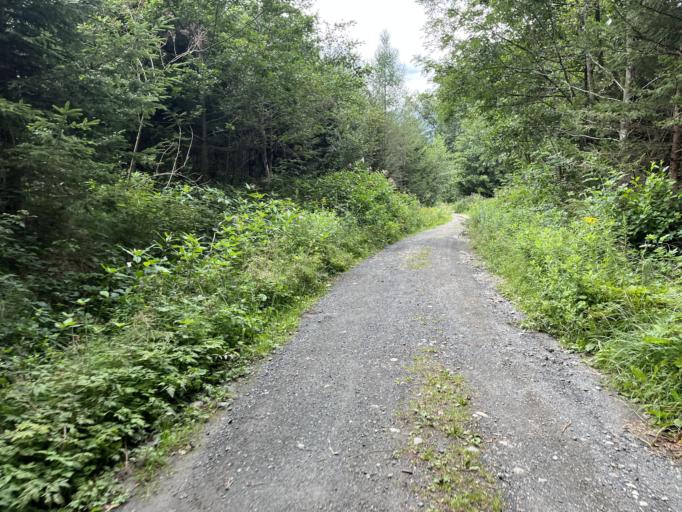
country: AT
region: Carinthia
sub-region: Politischer Bezirk Spittal an der Drau
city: Seeboden
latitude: 46.8045
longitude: 13.5272
